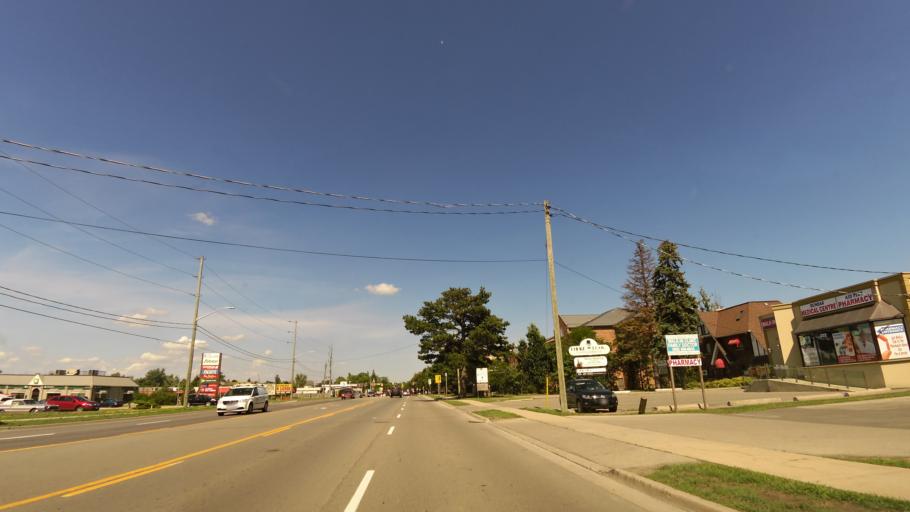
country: CA
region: Ontario
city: Burlington
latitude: 43.3292
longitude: -79.8976
